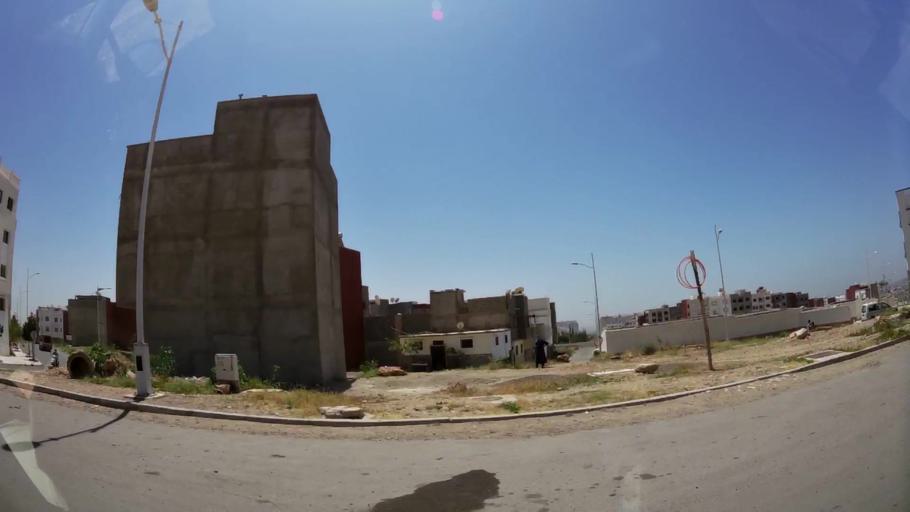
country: MA
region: Oued ed Dahab-Lagouira
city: Dakhla
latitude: 30.4450
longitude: -9.5581
